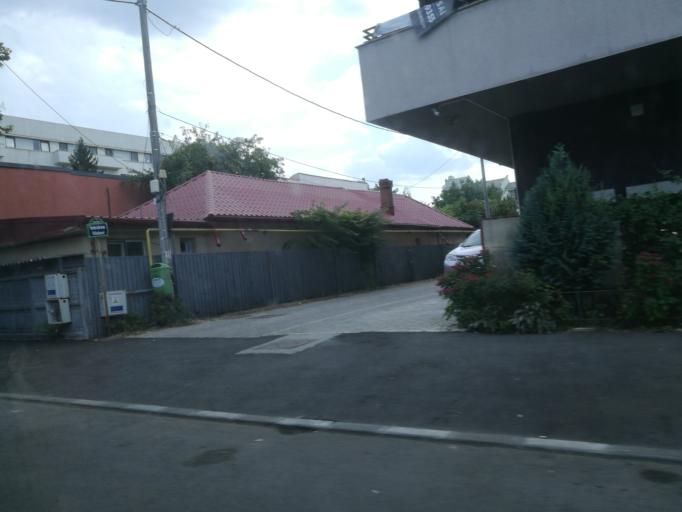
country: RO
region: Ilfov
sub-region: Comuna Otopeni
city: Otopeni
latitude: 44.4967
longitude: 26.0717
